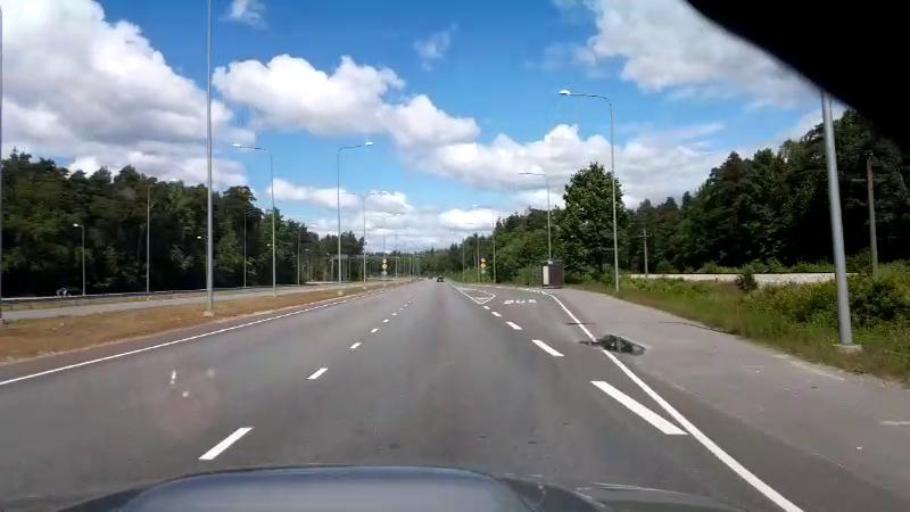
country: EE
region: Paernumaa
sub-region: Paernu linn
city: Parnu
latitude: 58.3835
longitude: 24.5569
